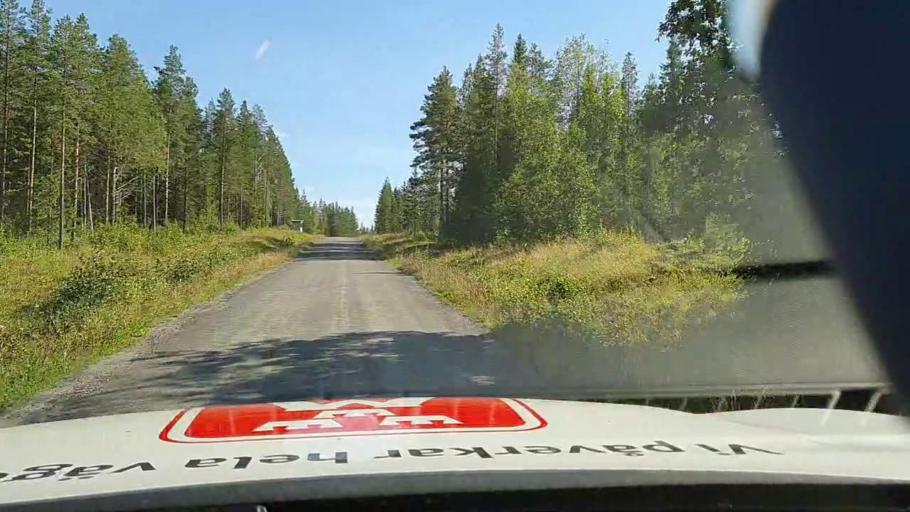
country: SE
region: Jaemtland
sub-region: OEstersunds Kommun
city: Lit
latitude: 63.7663
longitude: 14.6602
